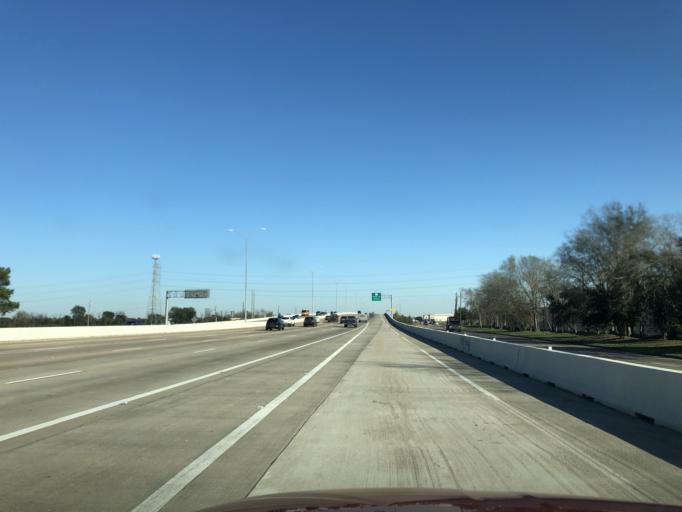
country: US
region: Texas
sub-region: Fort Bend County
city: Fresno
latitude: 29.5961
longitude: -95.4507
